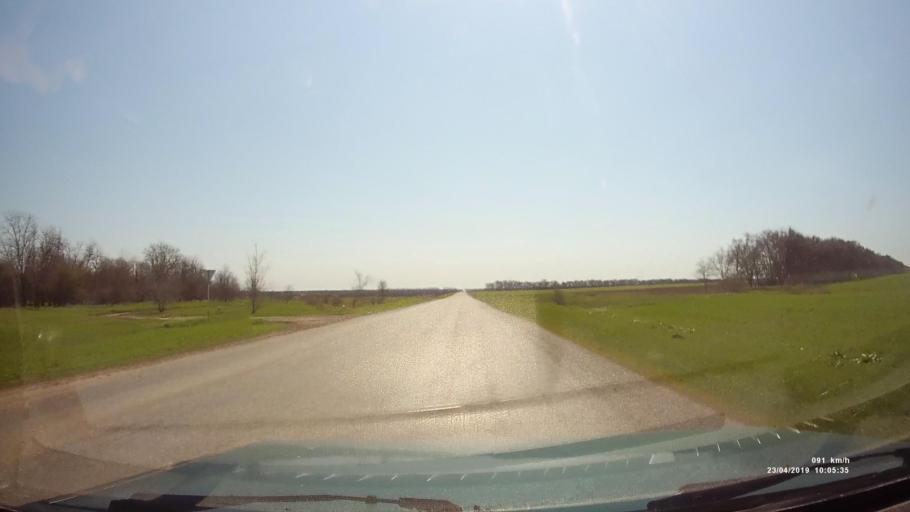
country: RU
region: Rostov
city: Sovetskoye
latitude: 46.7399
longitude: 42.2223
